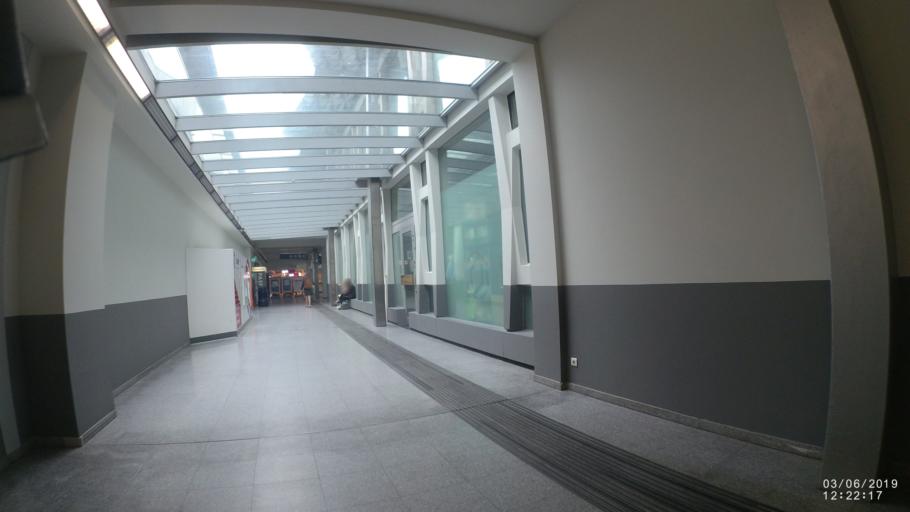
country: BE
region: Flanders
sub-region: Provincie Oost-Vlaanderen
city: Sint-Niklaas
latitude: 51.1725
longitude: 4.1432
